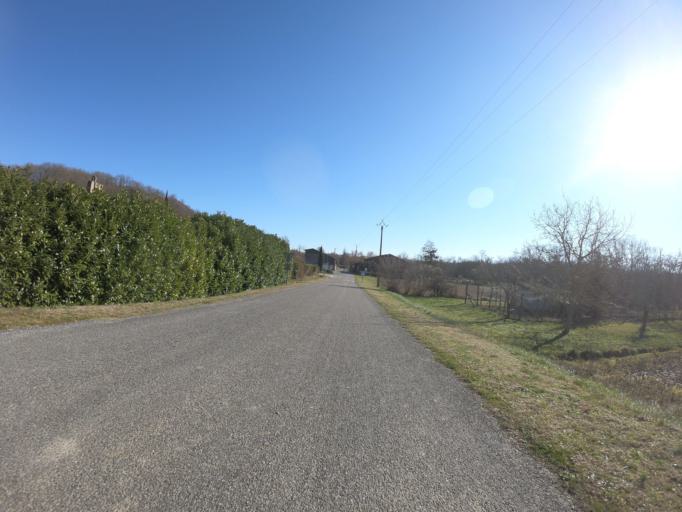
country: FR
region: Languedoc-Roussillon
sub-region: Departement de l'Aude
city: Belpech
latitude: 43.0957
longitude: 1.7591
